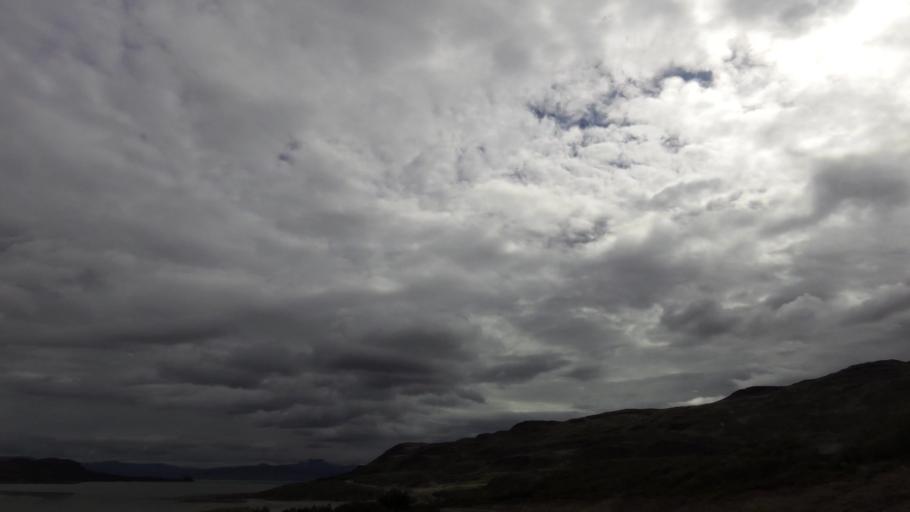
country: IS
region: West
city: Stykkisholmur
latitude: 65.5346
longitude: -22.1227
